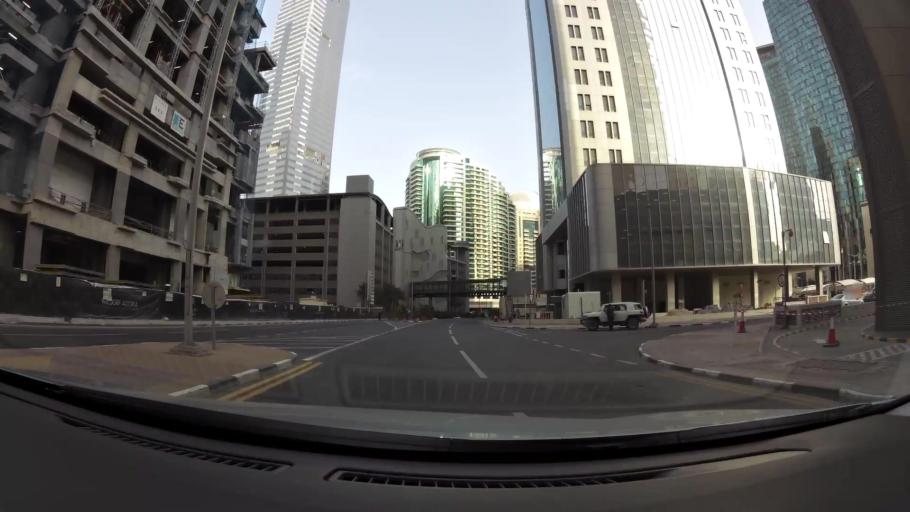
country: QA
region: Baladiyat ad Dawhah
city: Doha
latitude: 25.3271
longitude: 51.5327
